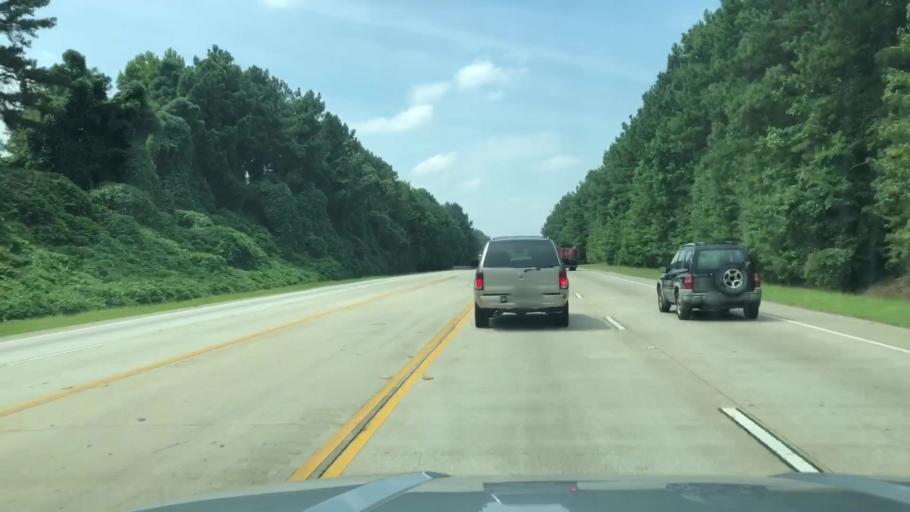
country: US
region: Georgia
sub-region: Cobb County
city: Powder Springs
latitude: 33.8382
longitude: -84.6825
